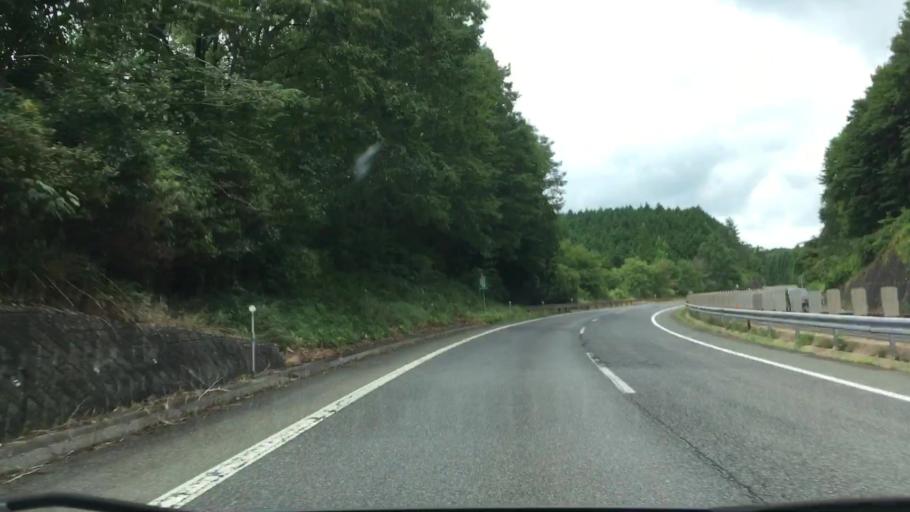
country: JP
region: Hiroshima
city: Shobara
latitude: 34.8926
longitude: 133.2151
